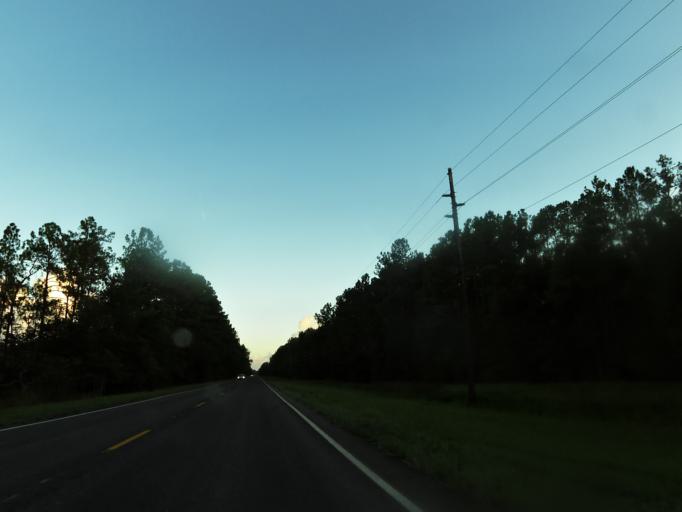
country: US
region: Georgia
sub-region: Camden County
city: Woodbine
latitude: 30.9928
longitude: -81.7300
